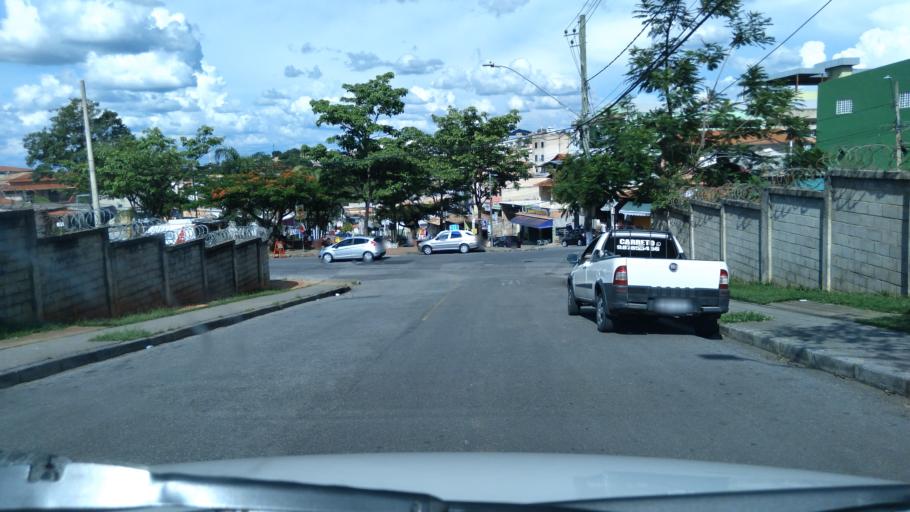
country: BR
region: Minas Gerais
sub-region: Belo Horizonte
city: Belo Horizonte
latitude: -19.8630
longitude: -43.8904
